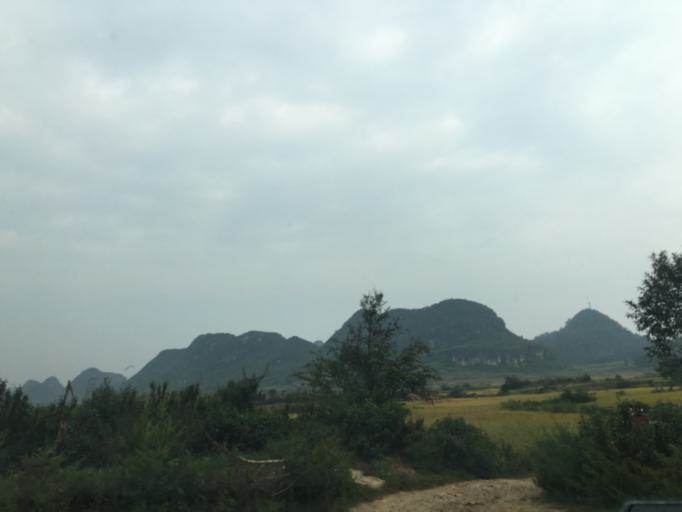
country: CN
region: Guangxi Zhuangzu Zizhiqu
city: Xinzhou
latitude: 25.4969
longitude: 105.6499
